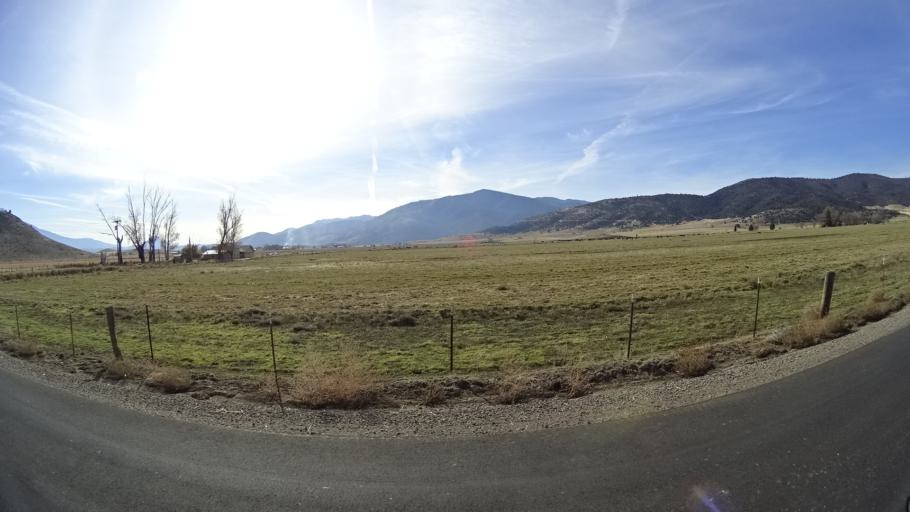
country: US
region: California
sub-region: Siskiyou County
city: Weed
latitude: 41.5381
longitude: -122.5291
